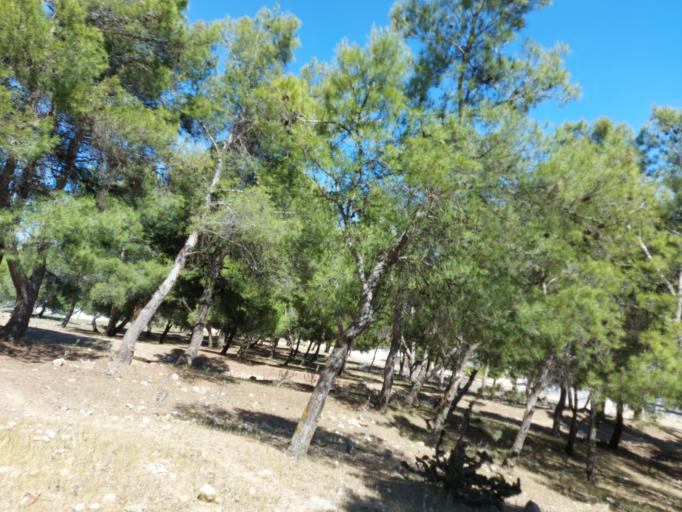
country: TN
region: Kef
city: El Kef
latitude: 36.1833
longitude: 8.7251
